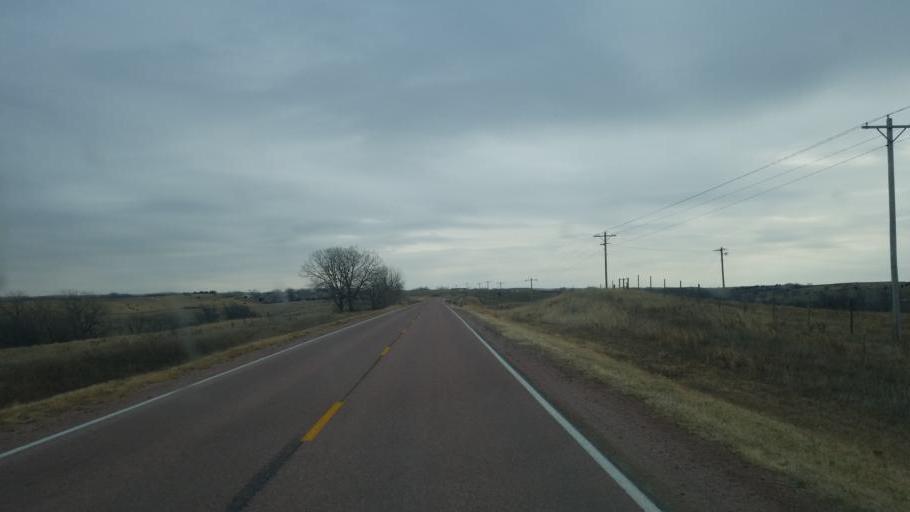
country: US
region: South Dakota
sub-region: Bon Homme County
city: Springfield
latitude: 42.7369
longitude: -97.9053
